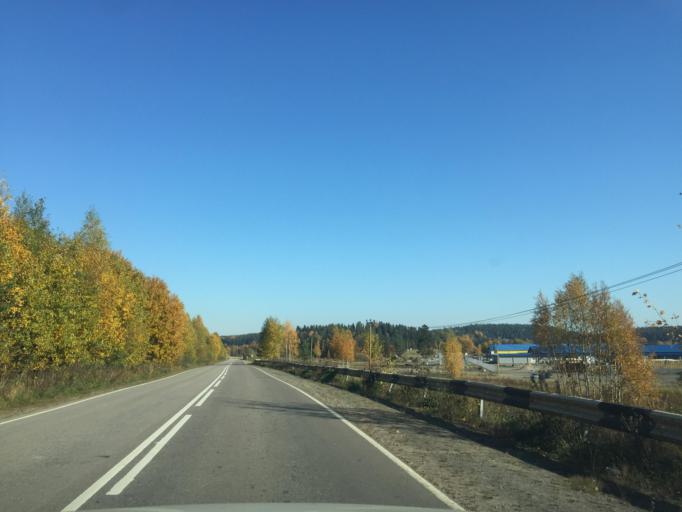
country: RU
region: Leningrad
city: Kuznechnoye
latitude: 61.3032
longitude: 29.9205
